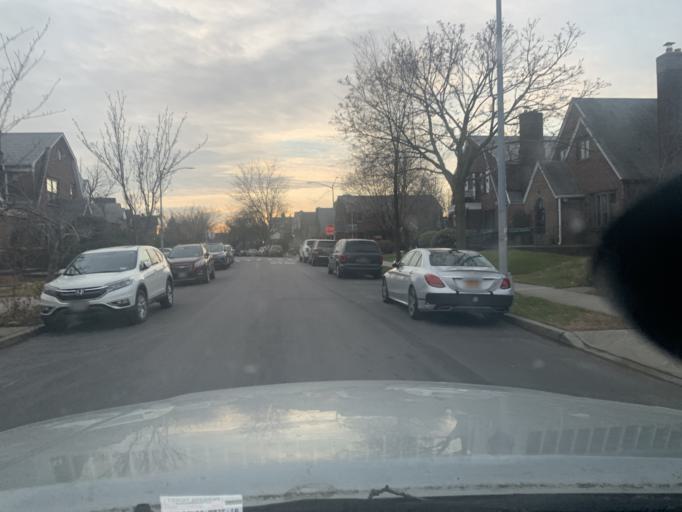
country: US
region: New York
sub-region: Queens County
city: Borough of Queens
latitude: 40.7224
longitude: -73.8657
